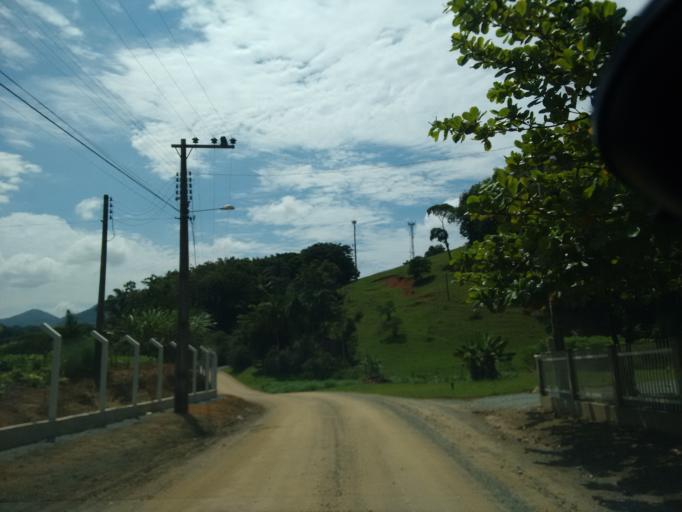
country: BR
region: Santa Catarina
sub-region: Indaial
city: Indaial
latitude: -26.8494
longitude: -49.1606
